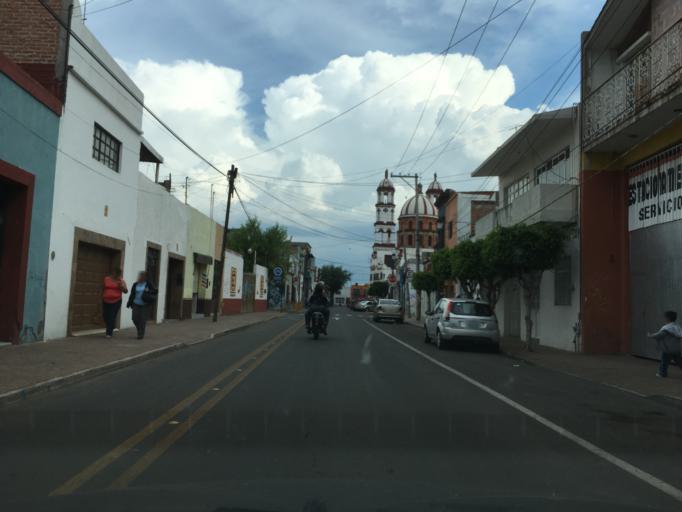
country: MX
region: Guanajuato
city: Celaya
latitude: 20.5251
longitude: -100.8176
